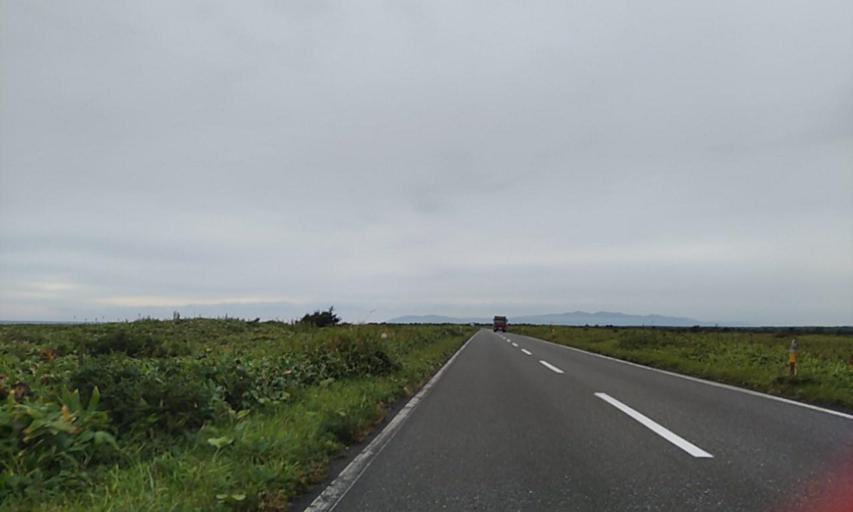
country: JP
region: Hokkaido
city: Makubetsu
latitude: 45.2606
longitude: 142.2461
